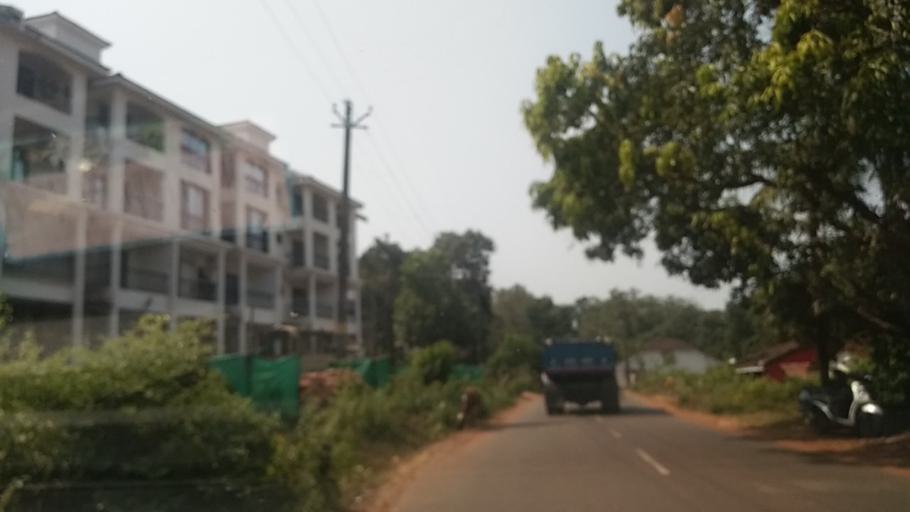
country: IN
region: Goa
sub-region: North Goa
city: Solim
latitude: 15.6161
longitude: 73.7879
